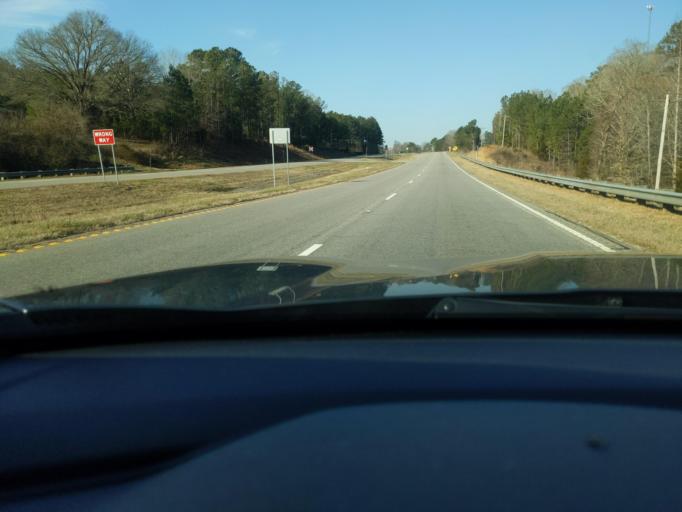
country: US
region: South Carolina
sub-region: Greenwood County
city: Greenwood
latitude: 34.1893
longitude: -82.2672
